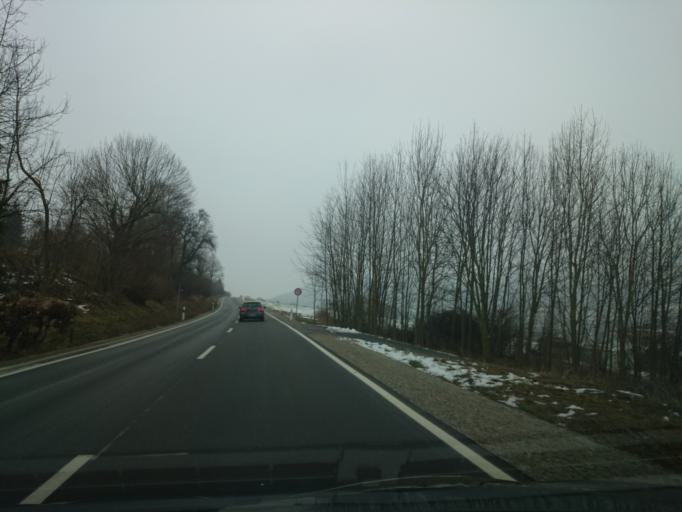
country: DE
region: Bavaria
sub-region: Regierungsbezirk Mittelfranken
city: Greding
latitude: 49.0513
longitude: 11.3413
